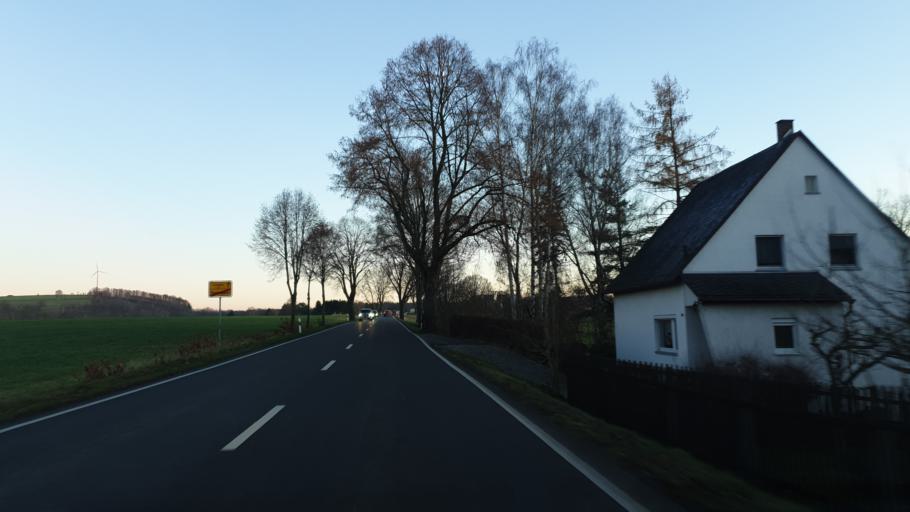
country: DE
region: Saxony
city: Oberlungwitz
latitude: 50.7778
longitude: 12.7040
